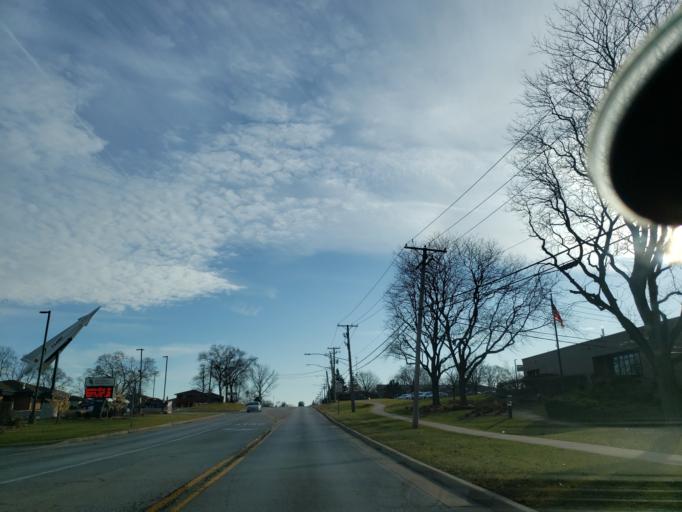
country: US
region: Illinois
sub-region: Cook County
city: Oak Forest
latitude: 41.6079
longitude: -87.7562
